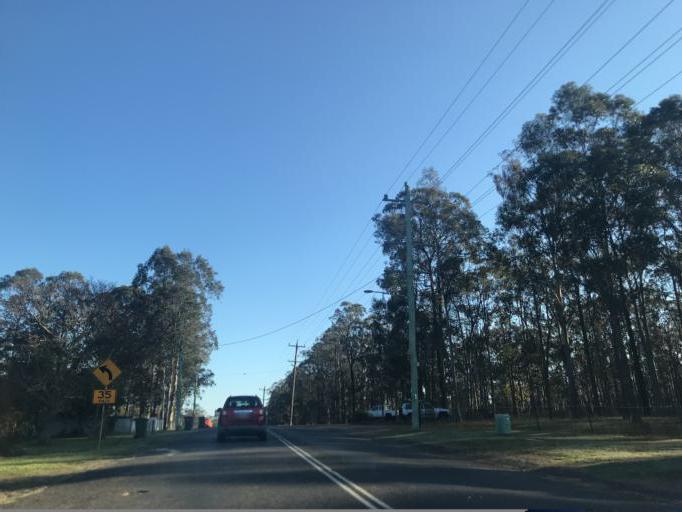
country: AU
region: New South Wales
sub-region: Cessnock
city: Cessnock
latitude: -32.8777
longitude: 151.3113
